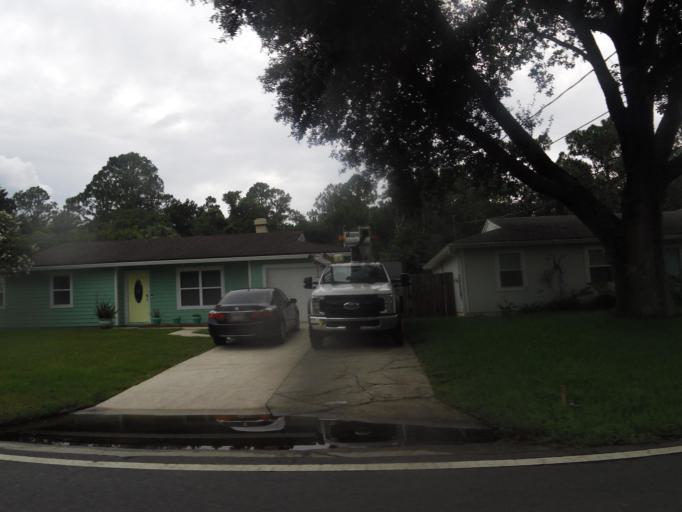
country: US
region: Florida
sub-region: Duval County
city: Jacksonville Beach
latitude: 30.2831
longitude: -81.4339
